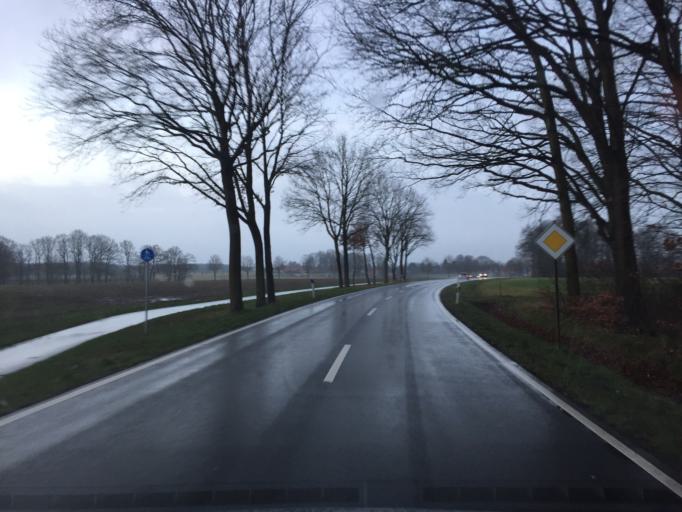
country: DE
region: Lower Saxony
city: Pennigsehl
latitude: 52.6526
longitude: 9.0320
